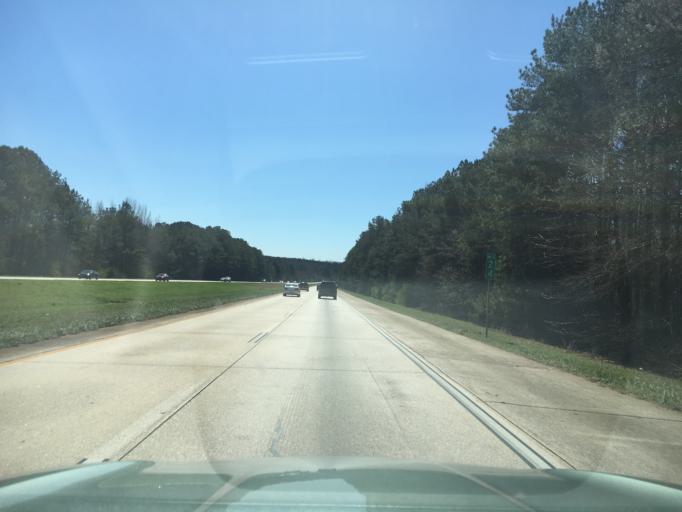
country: US
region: Georgia
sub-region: Troup County
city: Hogansville
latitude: 33.1059
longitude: -84.9065
